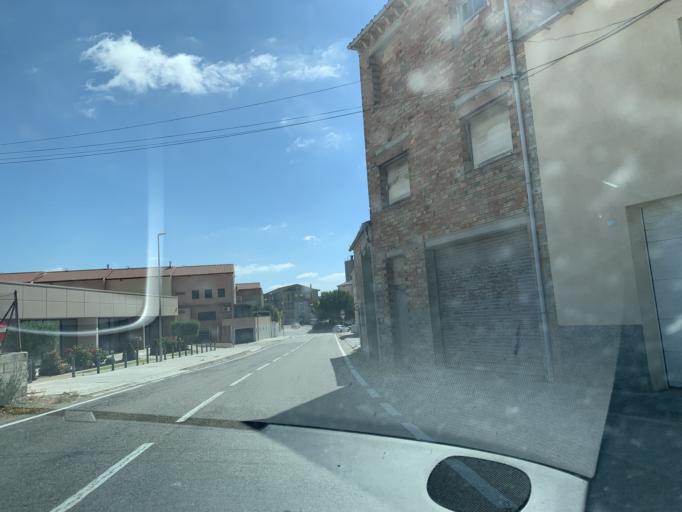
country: ES
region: Catalonia
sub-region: Provincia de Tarragona
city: Santa Coloma de Queralt
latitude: 41.5362
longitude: 1.3845
